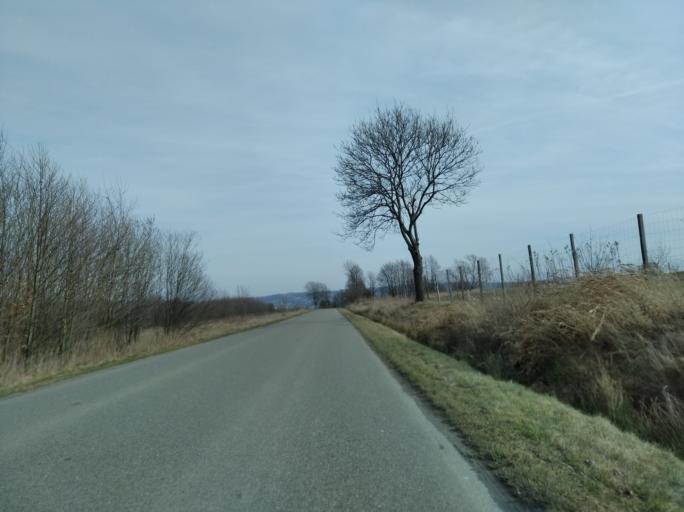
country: PL
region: Subcarpathian Voivodeship
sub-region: Powiat brzozowski
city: Stara Wies
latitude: 49.7135
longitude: 21.9931
